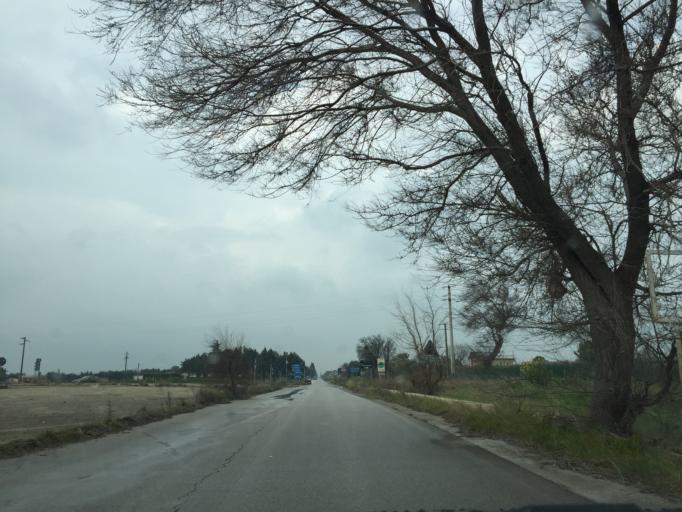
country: IT
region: Apulia
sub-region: Provincia di Foggia
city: Foggia
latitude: 41.4405
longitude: 15.4941
